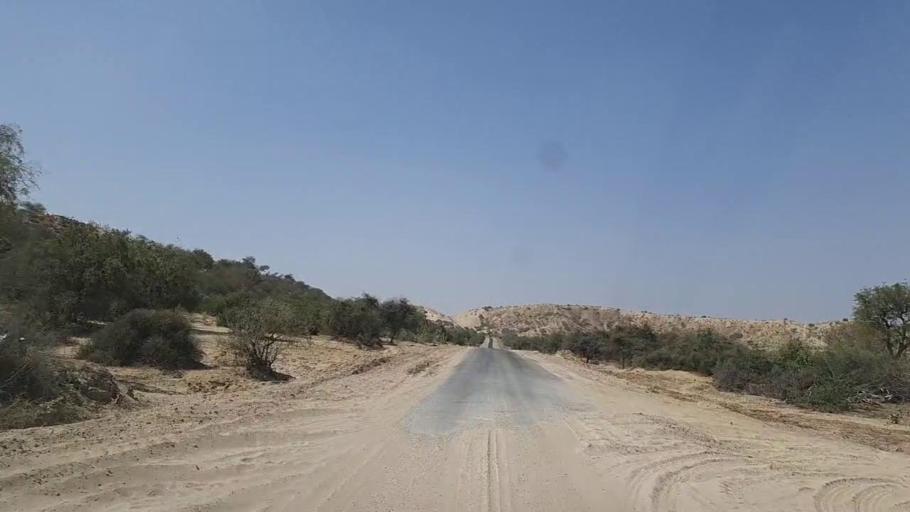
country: PK
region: Sindh
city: Diplo
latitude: 24.5853
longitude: 69.5256
